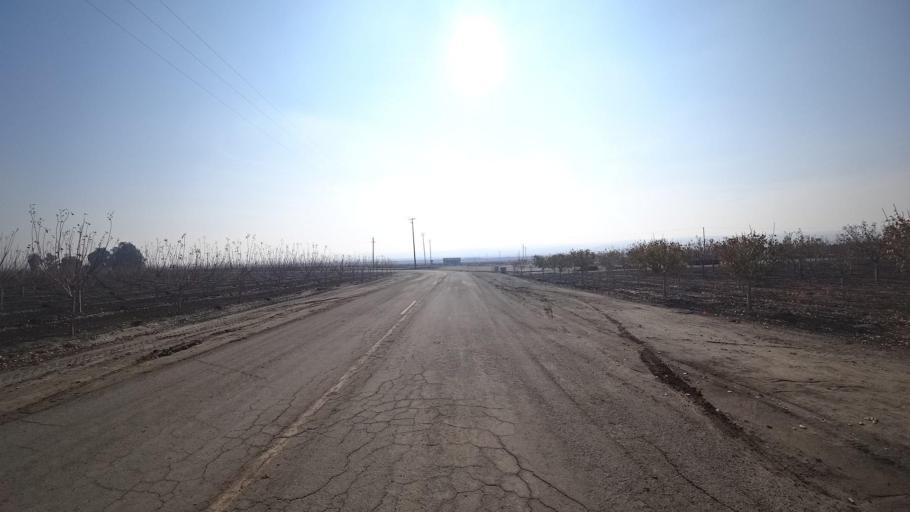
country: US
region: California
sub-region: Kern County
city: Buttonwillow
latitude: 35.3422
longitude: -119.4293
